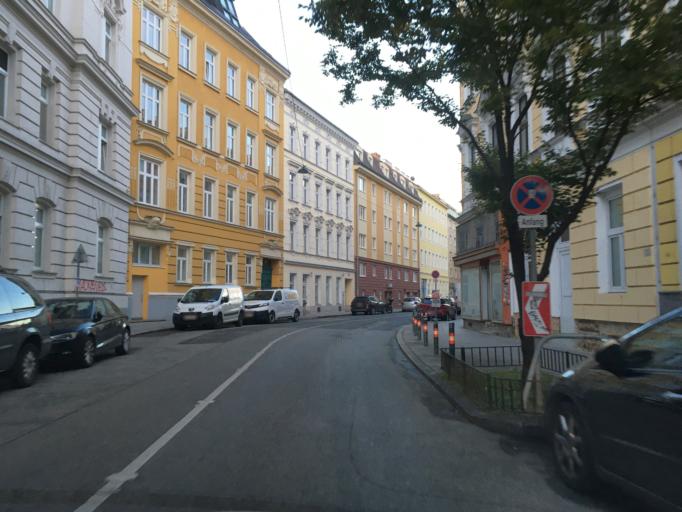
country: AT
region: Vienna
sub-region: Wien Stadt
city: Vienna
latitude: 48.1854
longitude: 16.3300
